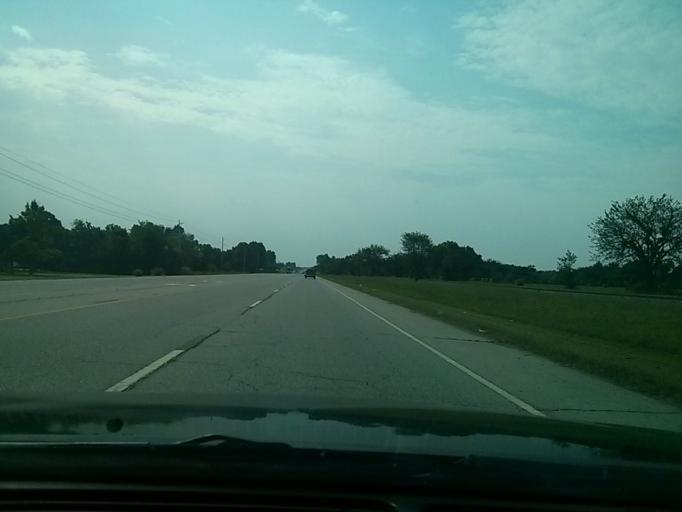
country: US
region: Oklahoma
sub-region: Wagoner County
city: Coweta
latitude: 35.9957
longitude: -95.6763
